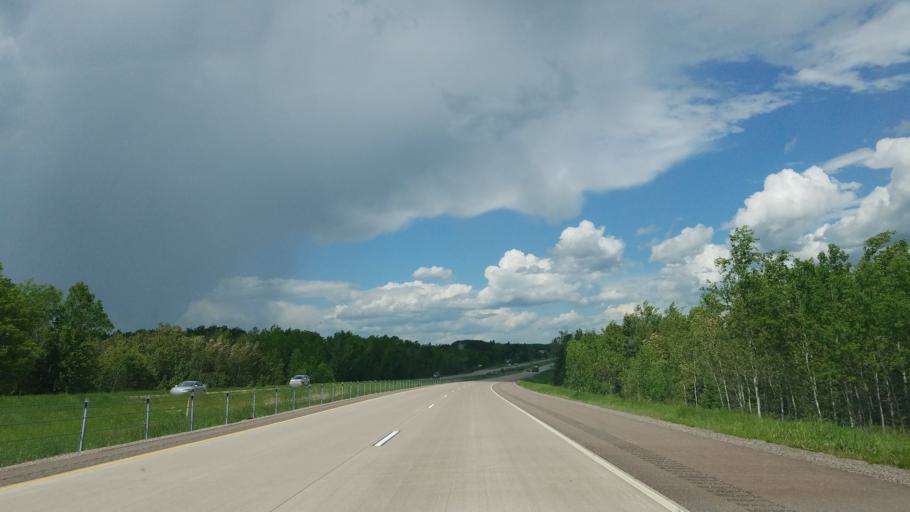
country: US
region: Minnesota
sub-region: Carlton County
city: Moose Lake
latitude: 46.4735
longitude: -92.7156
